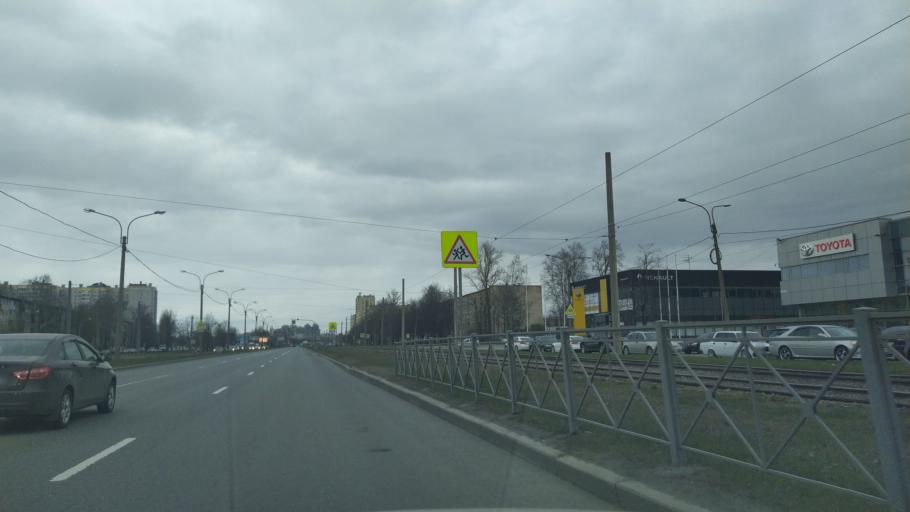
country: RU
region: Leningrad
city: Akademicheskoe
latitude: 60.0075
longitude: 30.4354
